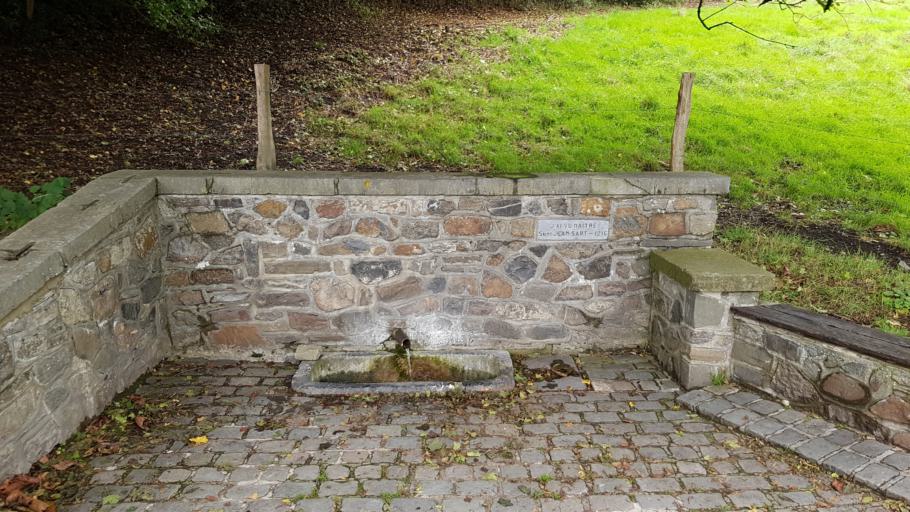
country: BE
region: Flanders
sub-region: Provincie Limburg
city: Sint-Pieters-Voeren
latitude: 50.7050
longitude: 5.8135
